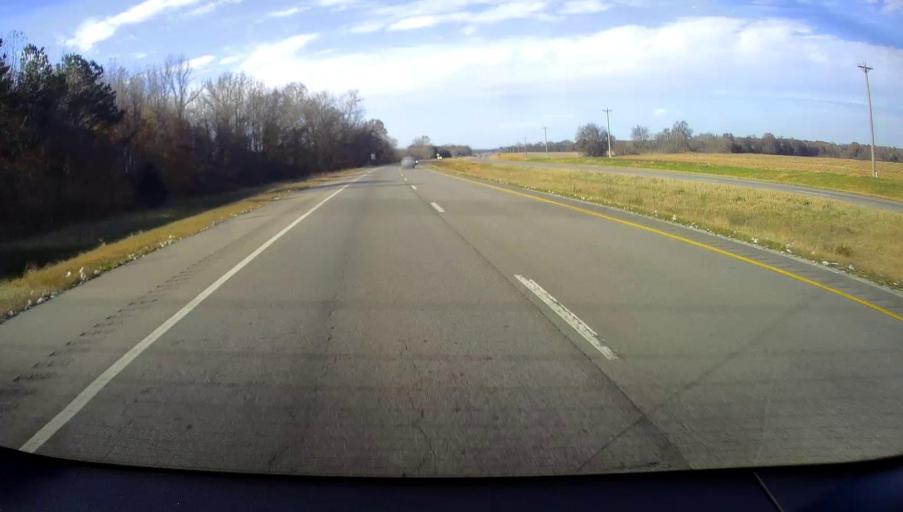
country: US
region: Alabama
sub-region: Lawrence County
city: Town Creek
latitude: 34.6616
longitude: -87.2806
